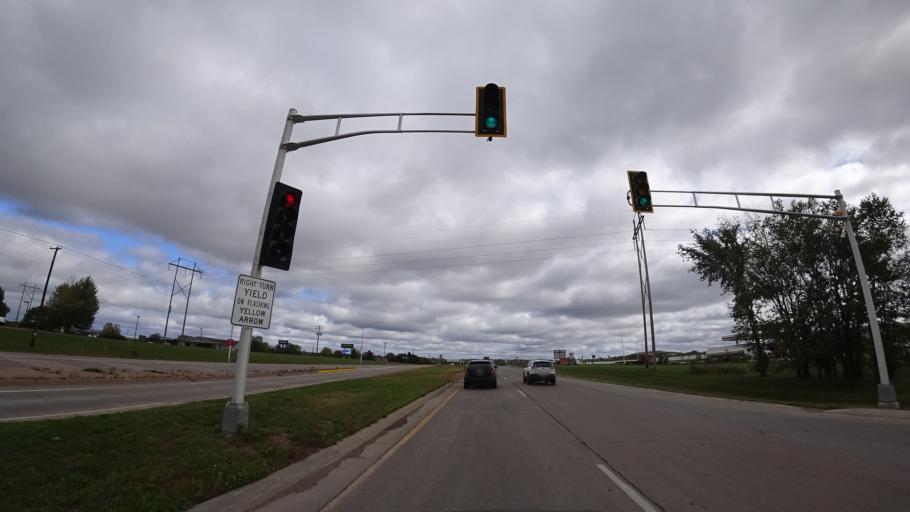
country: US
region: Wisconsin
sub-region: Eau Claire County
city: Eau Claire
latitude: 44.8434
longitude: -91.5894
